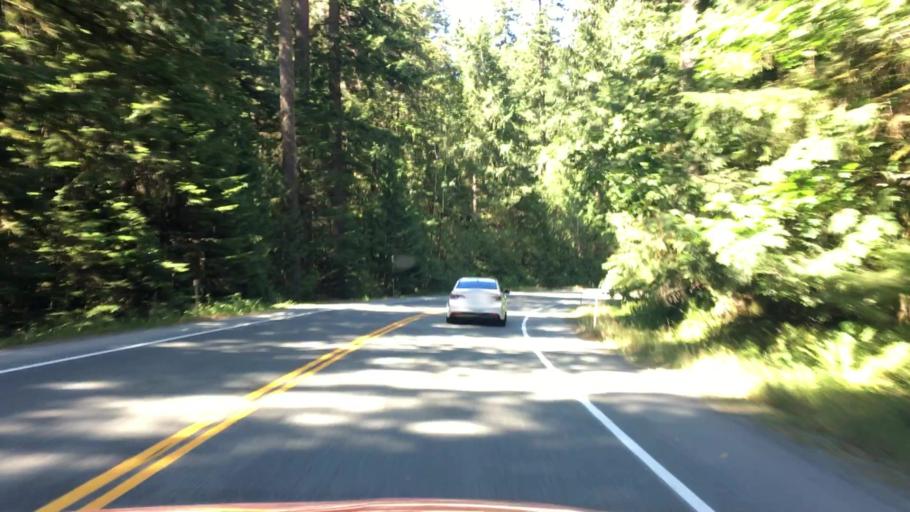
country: CA
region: British Columbia
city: Port Alberni
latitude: 49.2705
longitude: -124.6755
